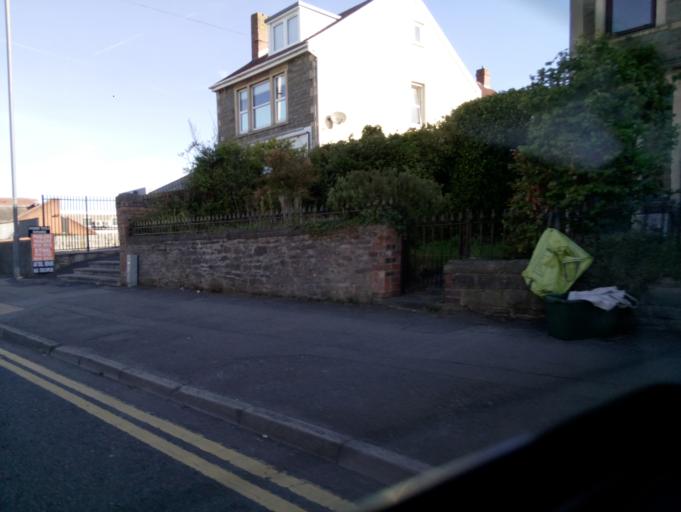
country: GB
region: England
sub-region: South Gloucestershire
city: Kingswood
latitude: 51.4477
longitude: -2.5120
